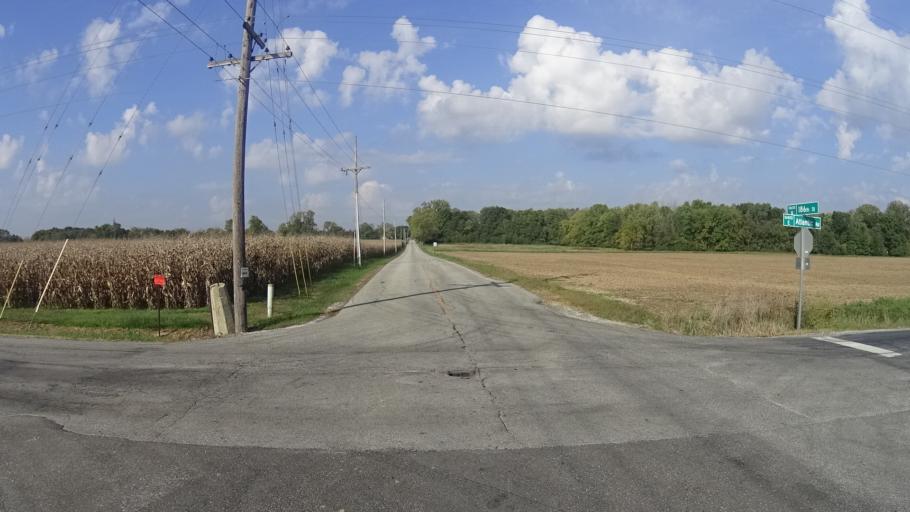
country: US
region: Indiana
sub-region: Madison County
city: Lapel
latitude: 40.0600
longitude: -85.8630
